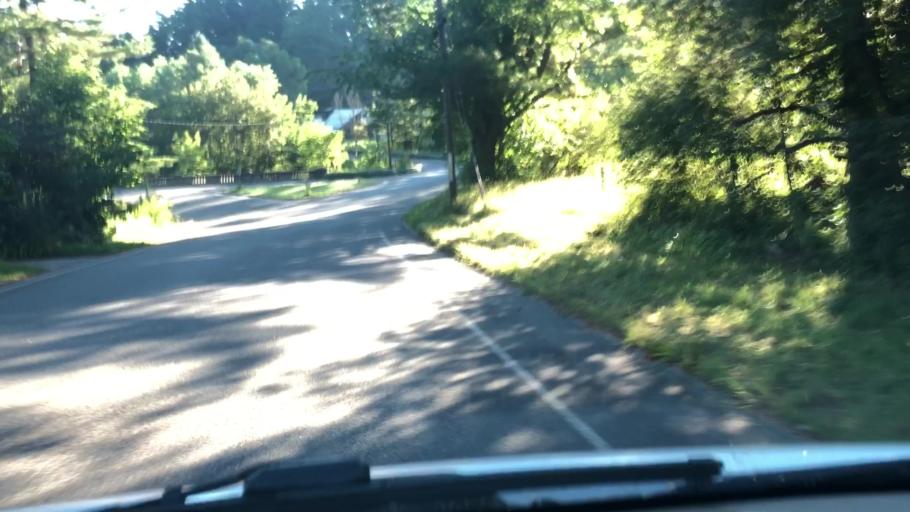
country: US
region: Massachusetts
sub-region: Berkshire County
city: Hinsdale
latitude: 42.4775
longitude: -72.9864
